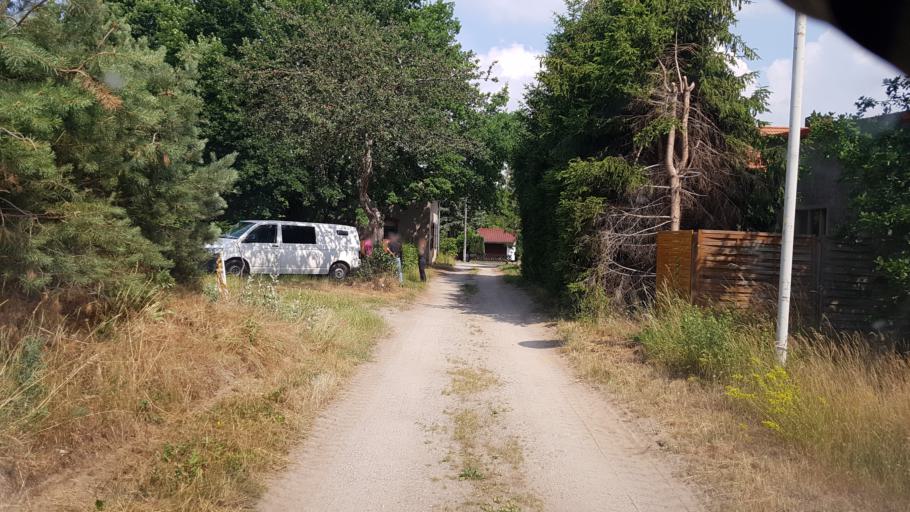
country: DE
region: Brandenburg
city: Doberlug-Kirchhain
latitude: 51.6357
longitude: 13.5378
